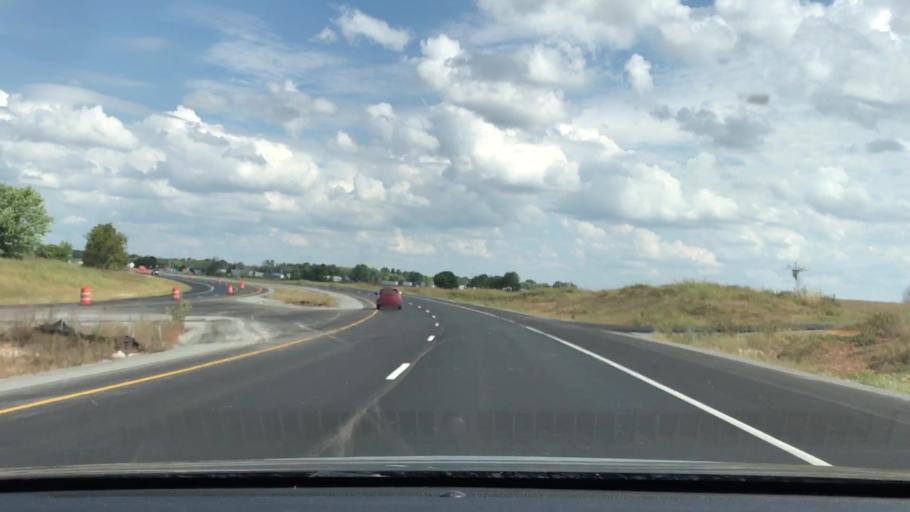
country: US
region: Kentucky
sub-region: Trigg County
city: Cadiz
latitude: 36.8617
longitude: -87.7990
